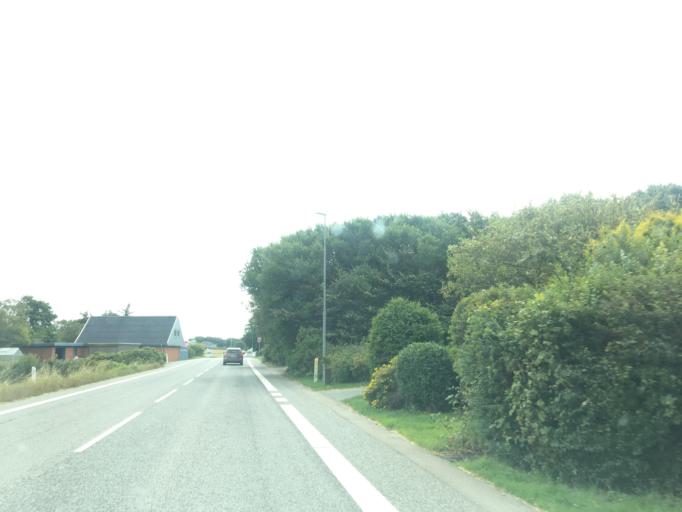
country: DK
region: North Denmark
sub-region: Thisted Kommune
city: Hurup
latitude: 56.7577
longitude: 8.3220
